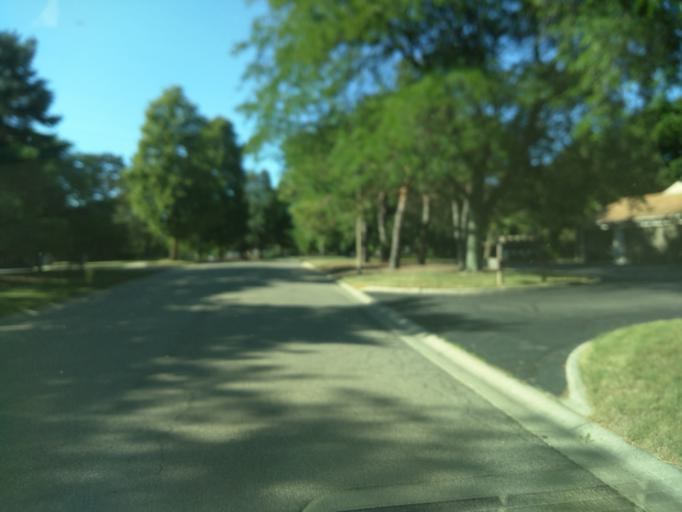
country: US
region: Michigan
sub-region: Eaton County
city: Waverly
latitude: 42.7235
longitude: -84.6350
